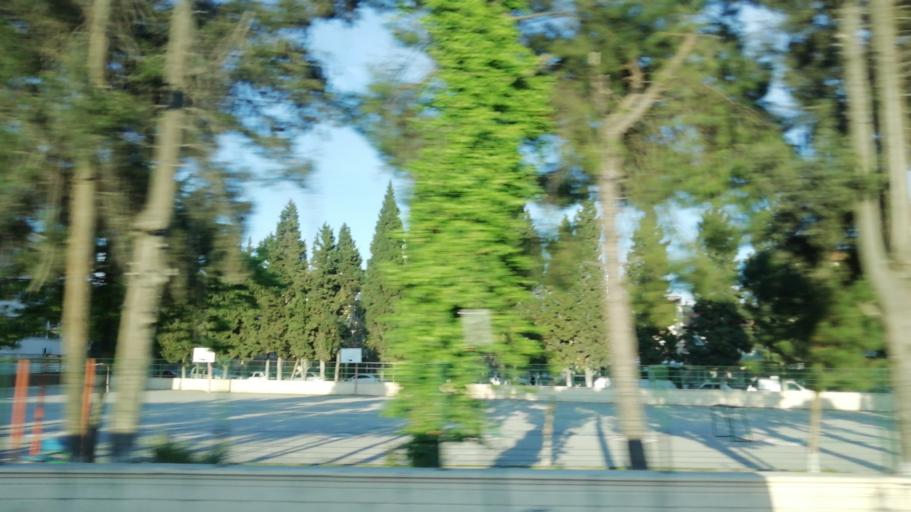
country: TR
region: Manisa
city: Akhisar
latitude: 38.9260
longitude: 27.8347
